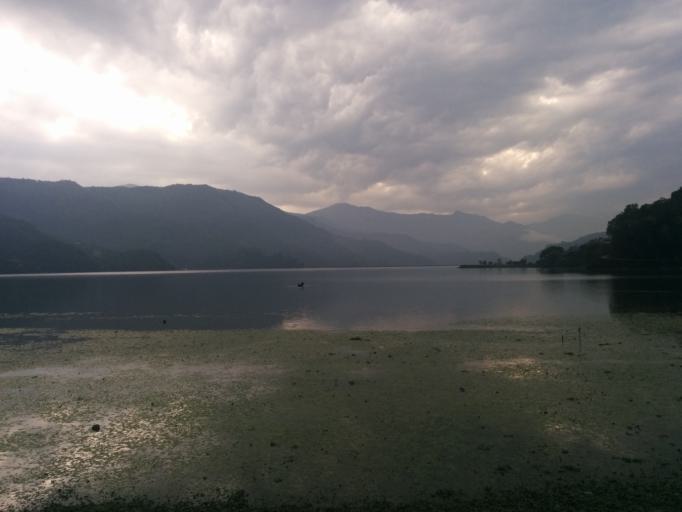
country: NP
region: Western Region
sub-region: Gandaki Zone
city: Pokhara
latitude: 28.2191
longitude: 83.9577
